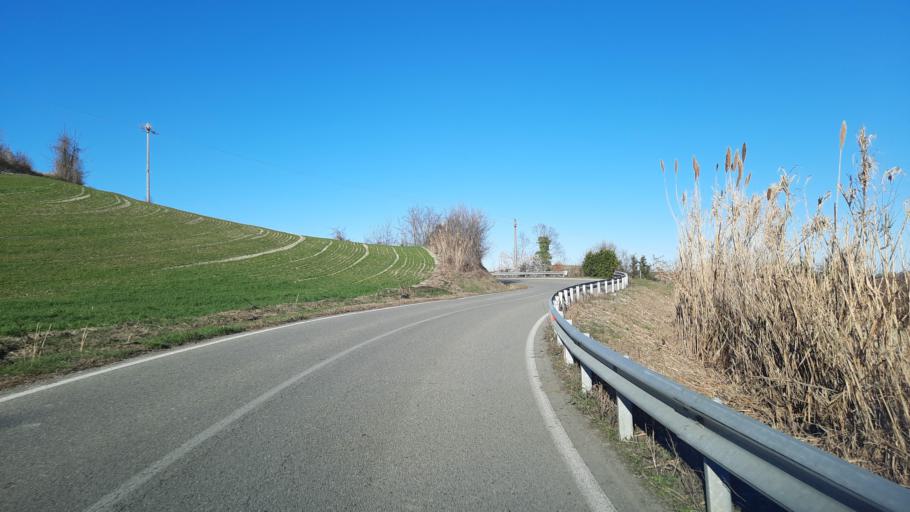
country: IT
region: Piedmont
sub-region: Provincia di Alessandria
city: Rosignano Monferrato
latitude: 45.0853
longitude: 8.4129
